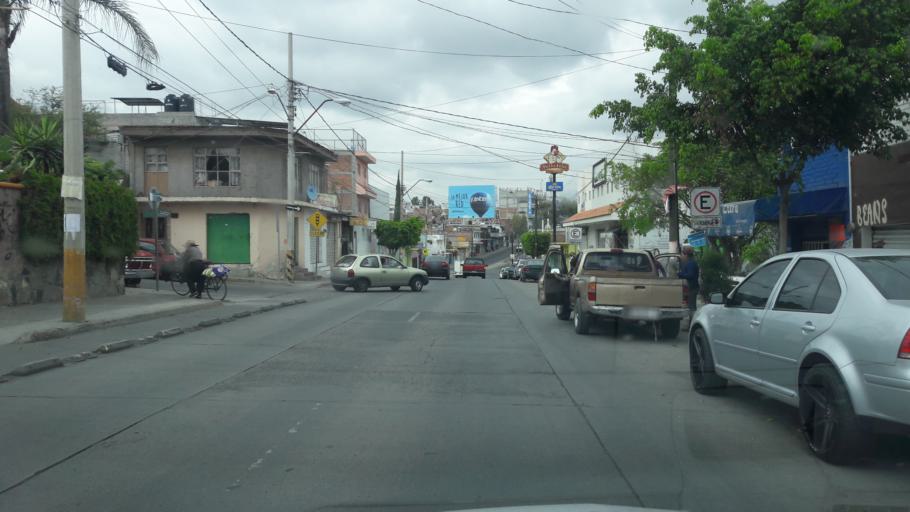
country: MX
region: Guanajuato
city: Leon
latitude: 21.1411
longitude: -101.7020
